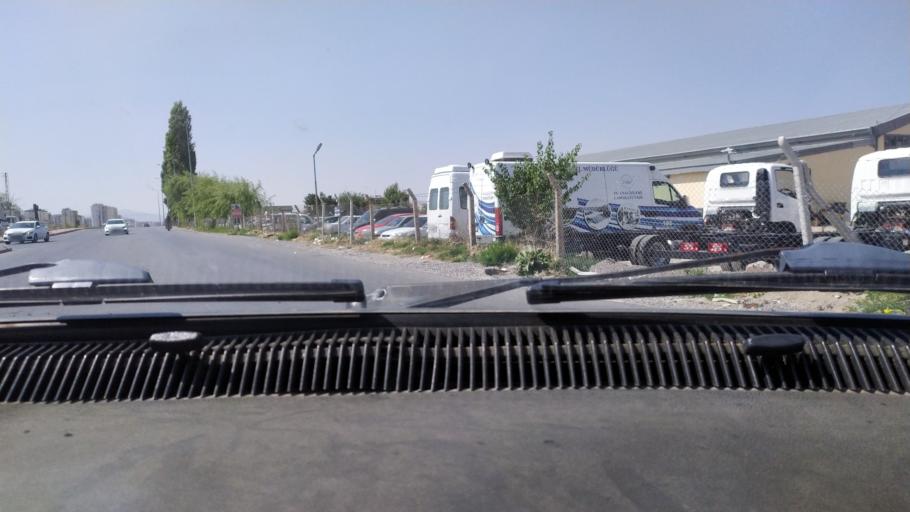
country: TR
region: Kayseri
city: Talas
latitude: 38.7196
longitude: 35.5550
